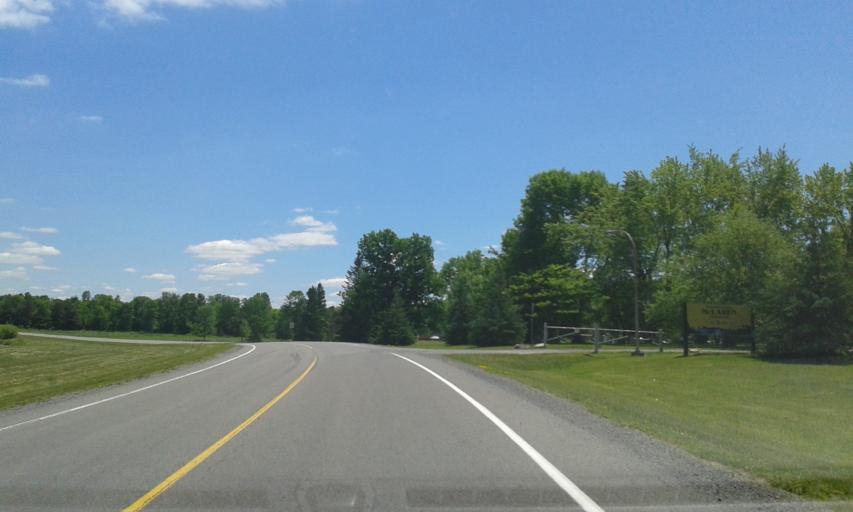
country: US
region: New York
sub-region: St. Lawrence County
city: Massena
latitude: 44.9916
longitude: -74.9691
